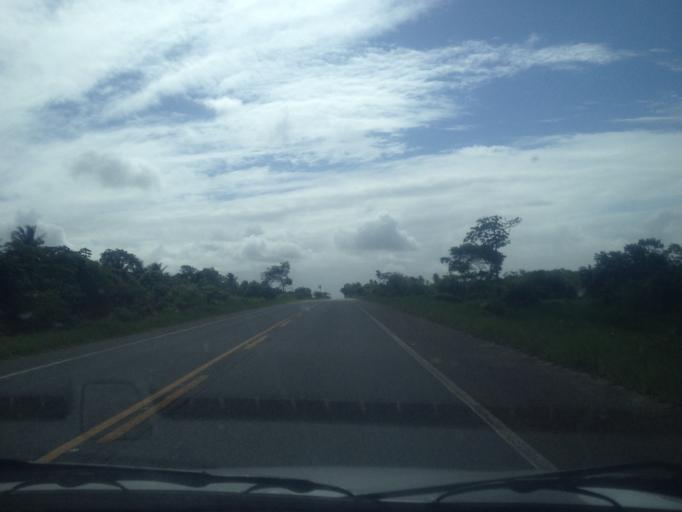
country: BR
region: Bahia
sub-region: Conde
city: Conde
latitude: -11.8441
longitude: -37.6353
